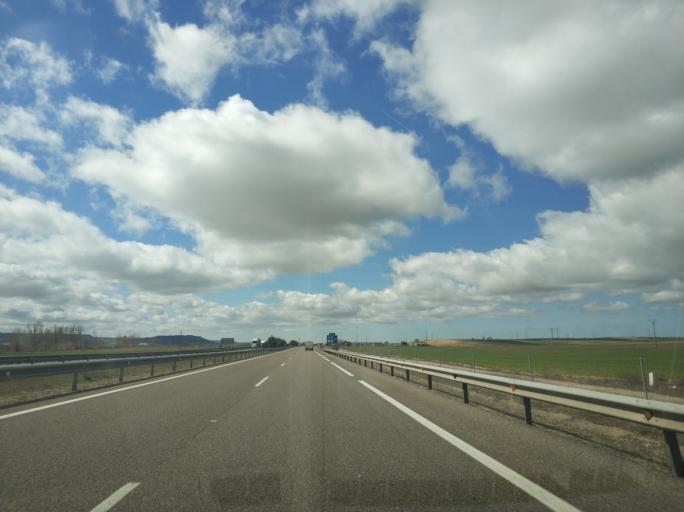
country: ES
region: Castille and Leon
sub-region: Provincia de Palencia
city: Torquemada
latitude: 42.0221
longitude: -4.3352
